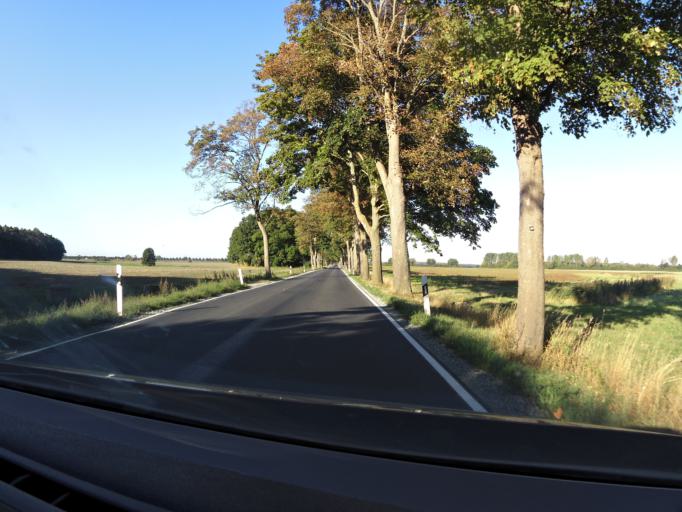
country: DE
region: Mecklenburg-Vorpommern
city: Alt-Sanitz
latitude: 53.8099
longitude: 13.4450
